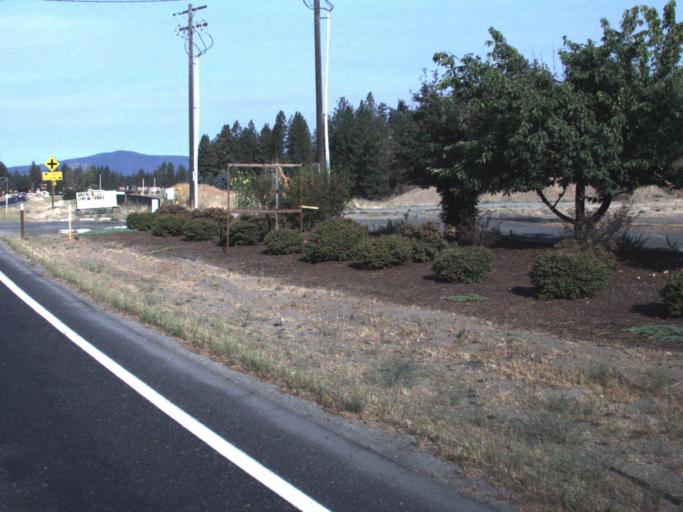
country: US
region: Washington
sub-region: Spokane County
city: Fairwood
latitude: 47.8117
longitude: -117.5665
